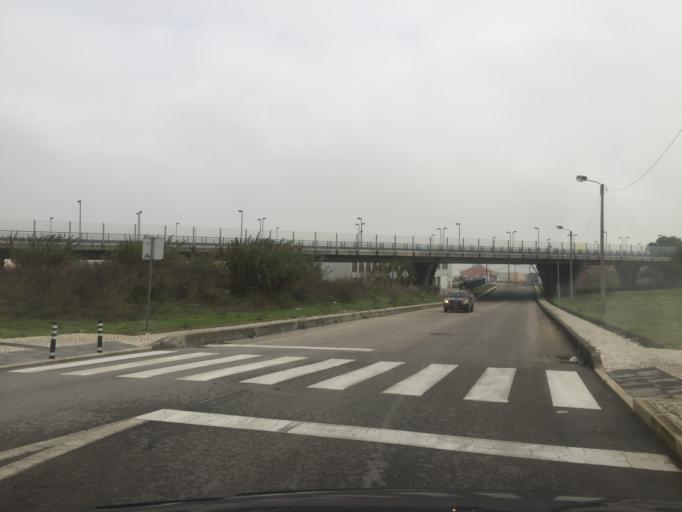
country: PT
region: Lisbon
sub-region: Odivelas
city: Olival do Basto
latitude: 38.7880
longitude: -9.1451
